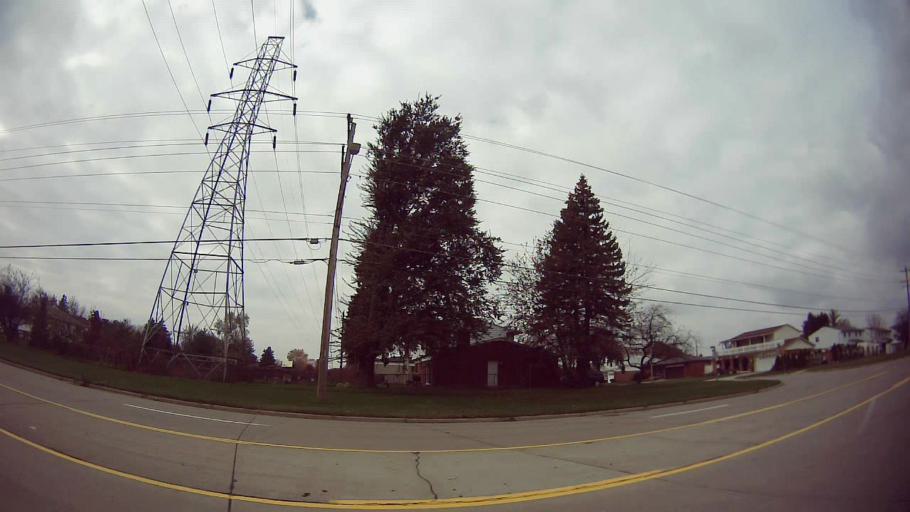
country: US
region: Michigan
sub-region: Oakland County
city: Madison Heights
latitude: 42.5241
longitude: -83.0680
